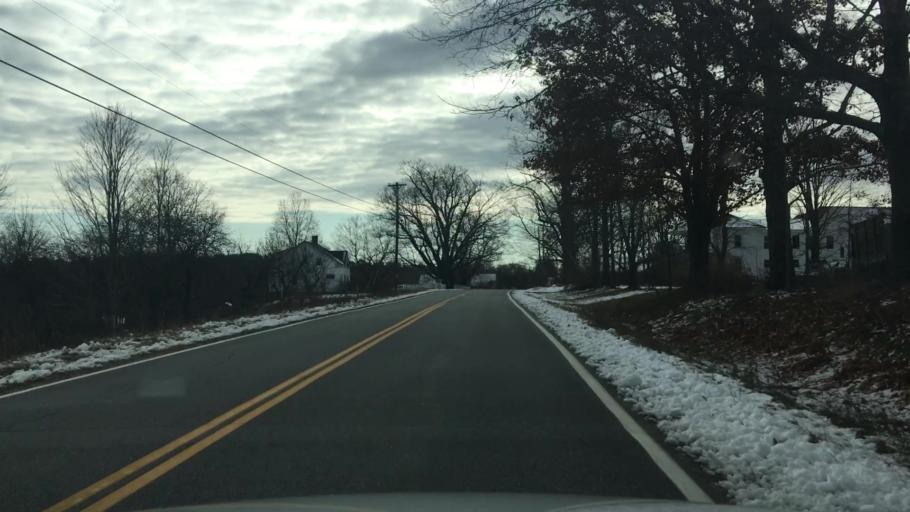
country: US
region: Maine
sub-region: Androscoggin County
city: Livermore
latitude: 44.3782
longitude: -70.2062
